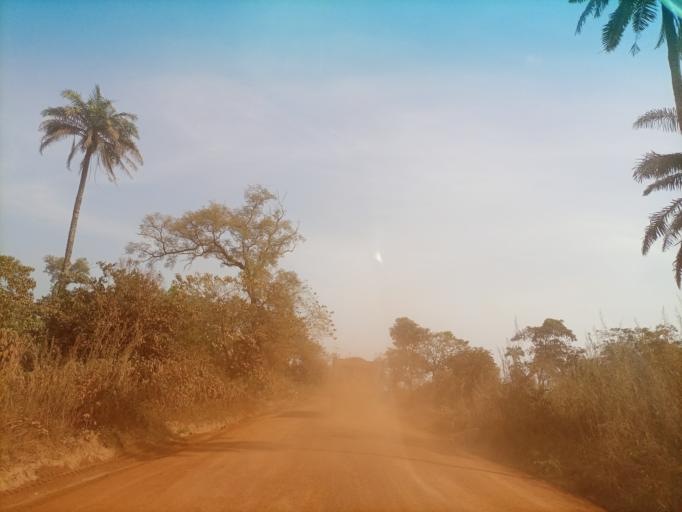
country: NG
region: Enugu
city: Eha Amufu
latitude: 6.6662
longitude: 7.7542
